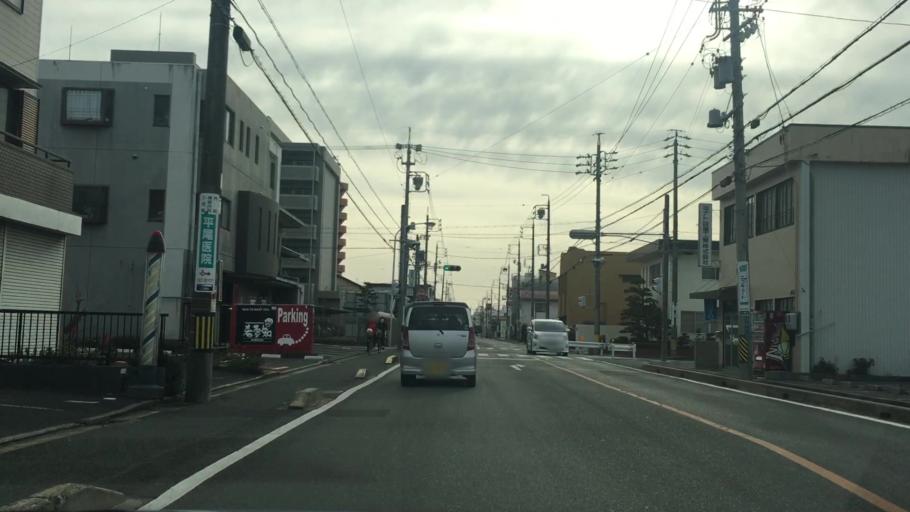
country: JP
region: Aichi
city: Toyohashi
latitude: 34.7577
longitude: 137.3953
